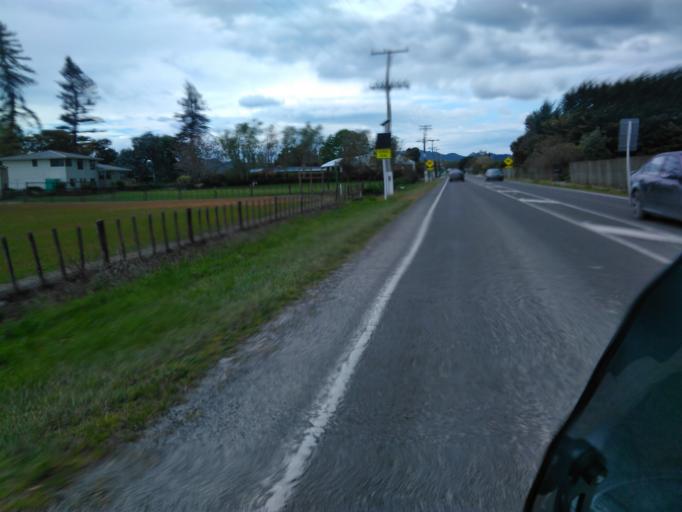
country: NZ
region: Gisborne
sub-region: Gisborne District
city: Gisborne
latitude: -38.6522
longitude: 177.9589
